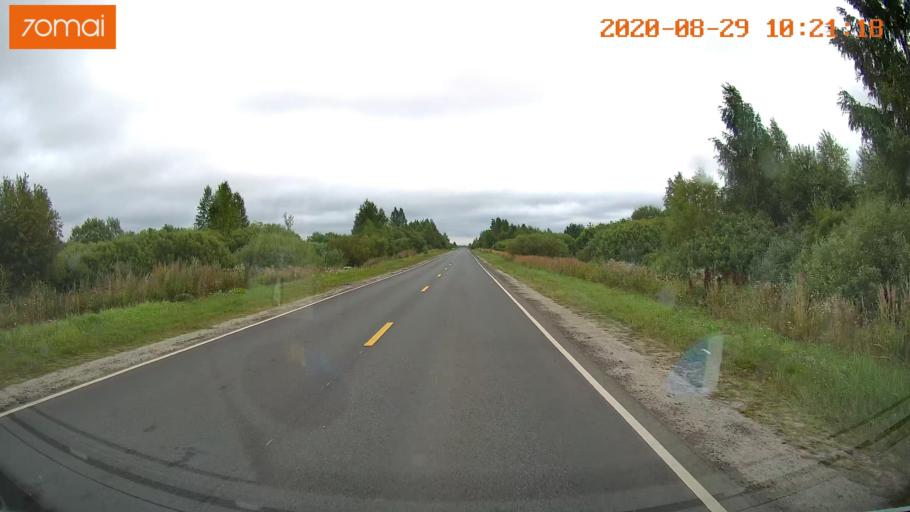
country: RU
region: Ivanovo
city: Yur'yevets
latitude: 57.3229
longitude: 42.9154
